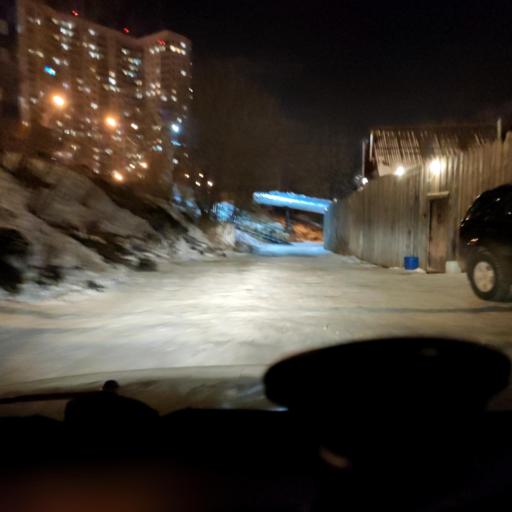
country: RU
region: Perm
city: Perm
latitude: 57.9893
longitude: 56.2682
